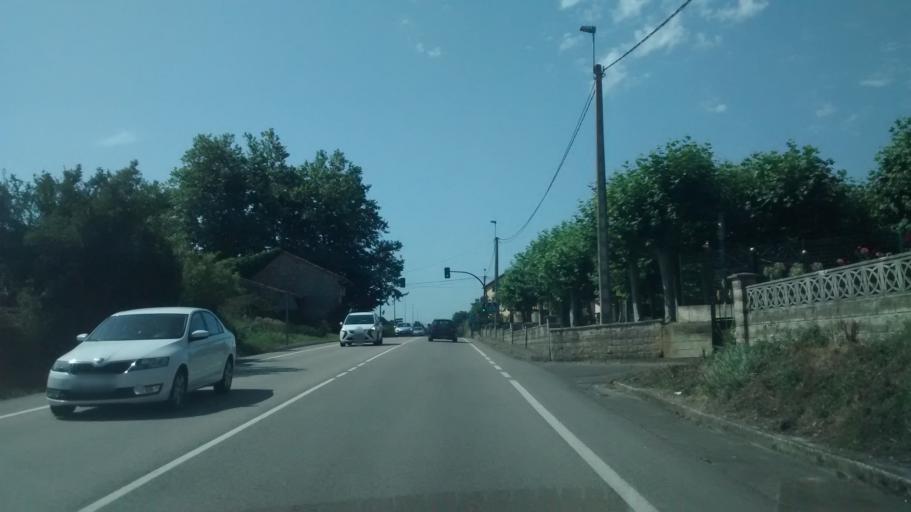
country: ES
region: Cantabria
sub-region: Provincia de Cantabria
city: Arnuero
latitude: 43.4579
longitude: -3.5524
